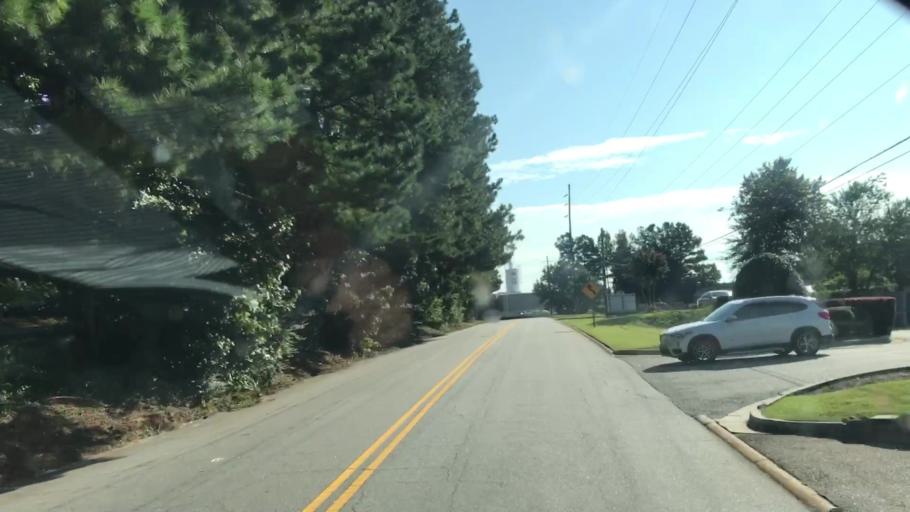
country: US
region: Georgia
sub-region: Gwinnett County
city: Lawrenceville
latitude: 33.9698
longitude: -83.9796
